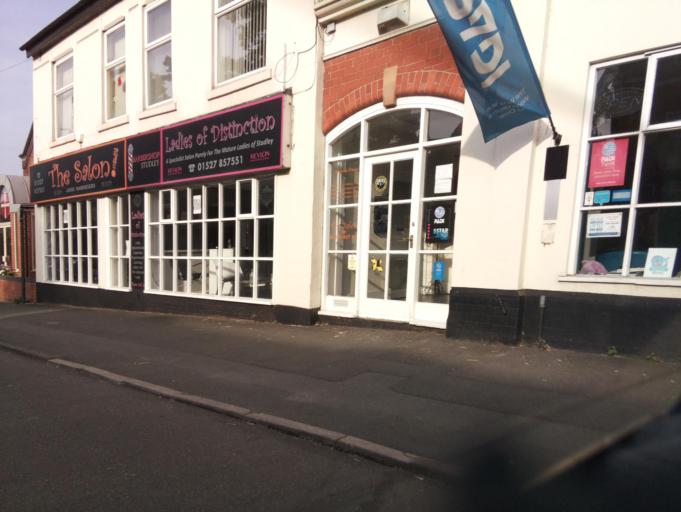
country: GB
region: England
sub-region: Warwickshire
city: Studley
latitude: 52.2719
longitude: -1.8943
